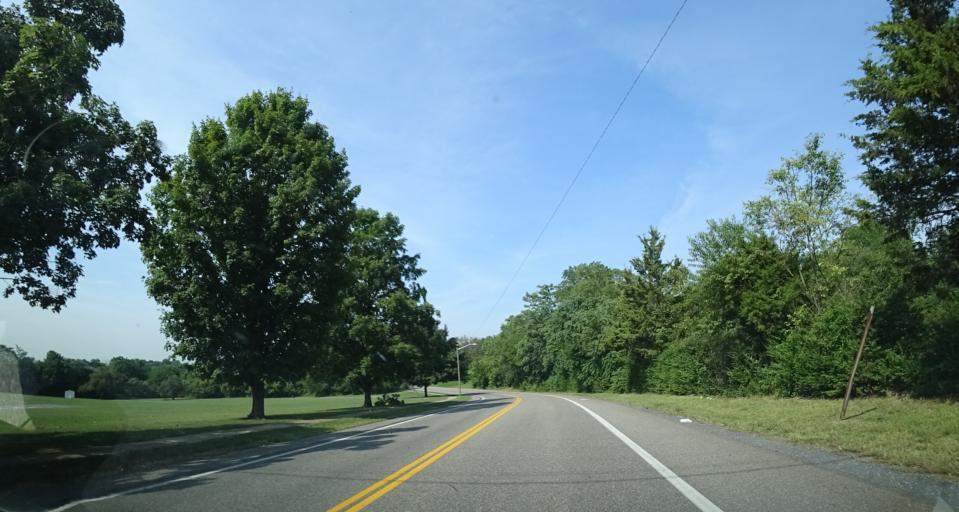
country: US
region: Virginia
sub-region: City of Harrisonburg
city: Harrisonburg
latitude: 38.4387
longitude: -78.8841
